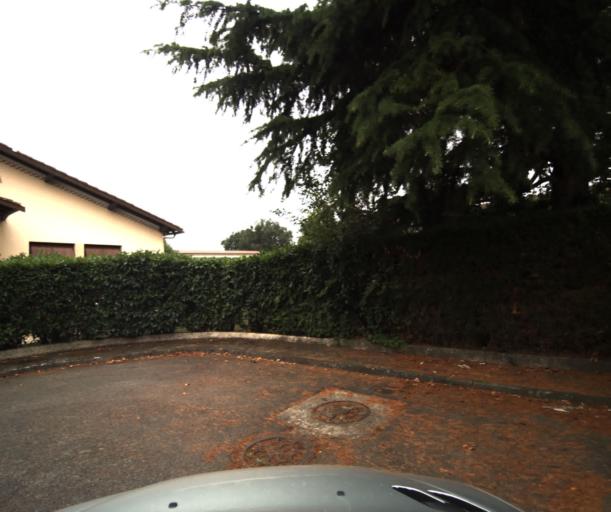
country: FR
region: Midi-Pyrenees
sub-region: Departement de la Haute-Garonne
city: Portet-sur-Garonne
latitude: 43.5219
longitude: 1.4029
